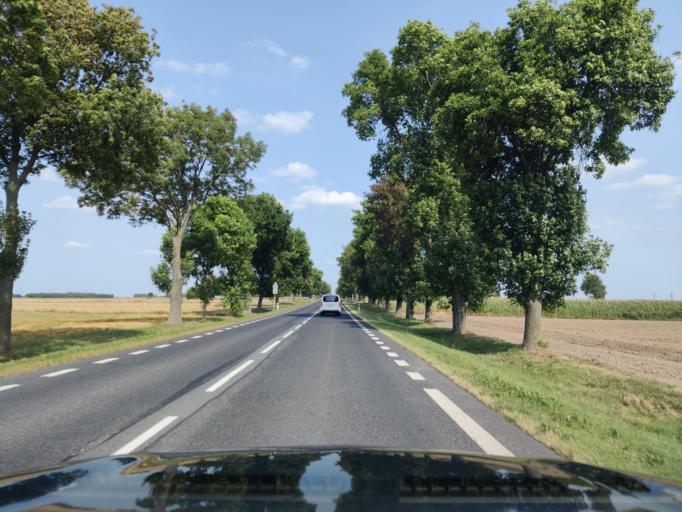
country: PL
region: Masovian Voivodeship
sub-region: Powiat makowski
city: Rzewnie
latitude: 52.8616
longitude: 21.3181
